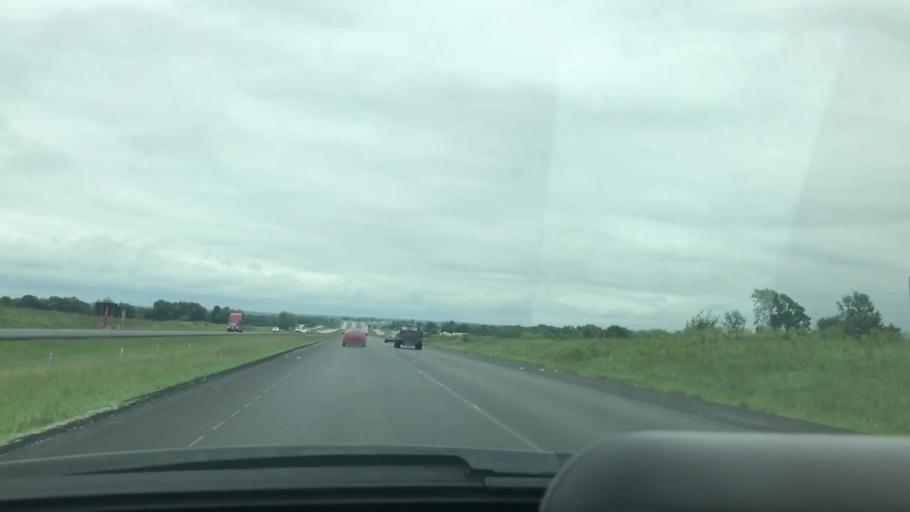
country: US
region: Missouri
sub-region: Lawrence County
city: Mount Vernon
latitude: 37.0746
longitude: -93.9246
